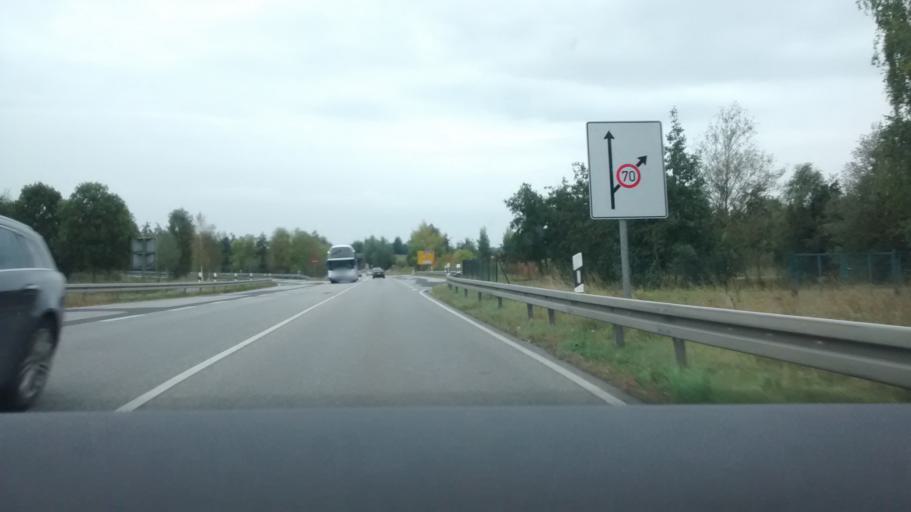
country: DE
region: Mecklenburg-Vorpommern
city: Wismar
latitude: 53.8803
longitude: 11.4226
